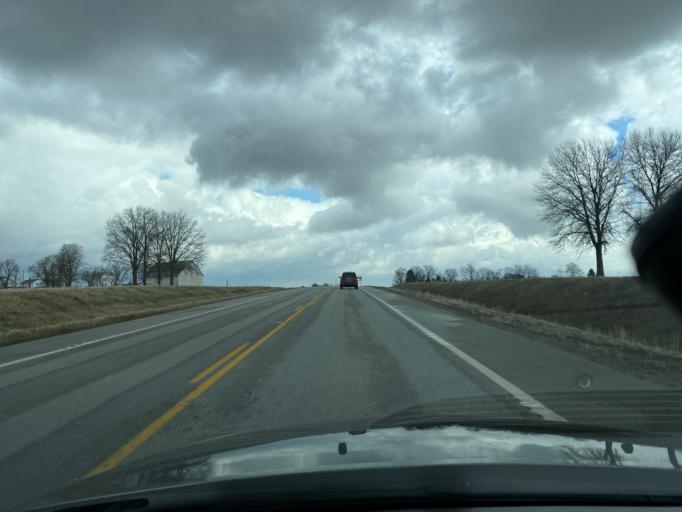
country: US
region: Ohio
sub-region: Wayne County
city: Smithville
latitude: 40.8410
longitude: -81.8930
